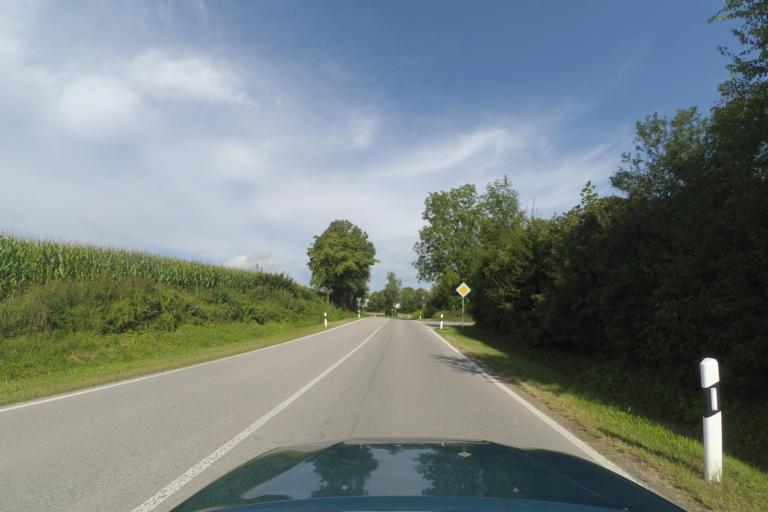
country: DE
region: Bavaria
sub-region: Lower Bavaria
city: Teugn
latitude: 48.9234
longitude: 12.0137
